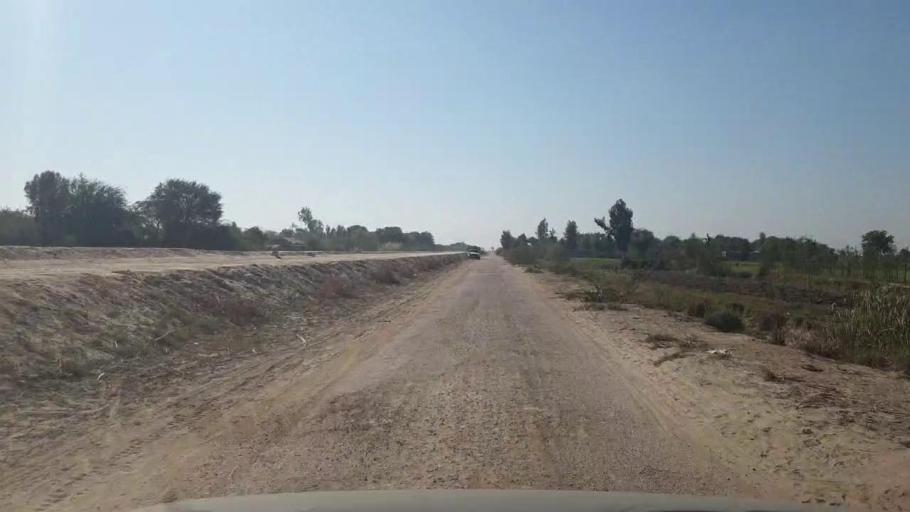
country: PK
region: Sindh
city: Mirwah Gorchani
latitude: 25.2989
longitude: 69.1030
